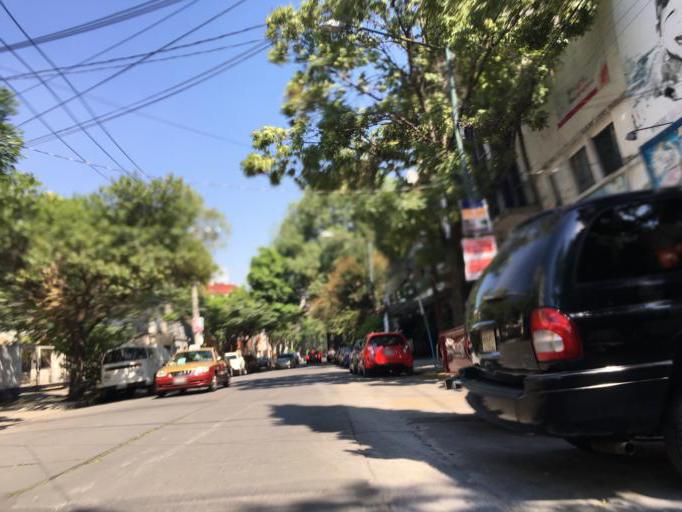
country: MX
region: Mexico City
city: Miguel Hidalgo
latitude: 19.4353
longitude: -99.1747
